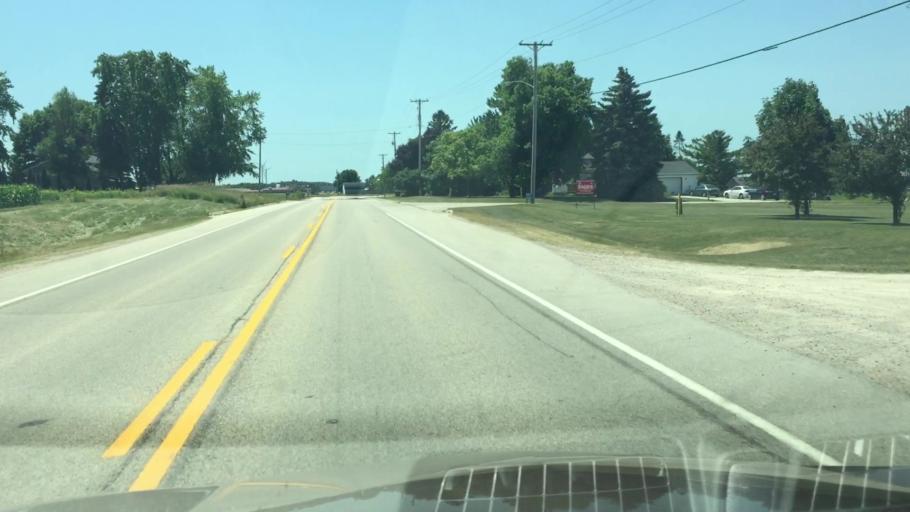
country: US
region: Wisconsin
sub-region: Fond du Lac County
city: Saint Peter
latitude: 43.9292
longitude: -88.3053
